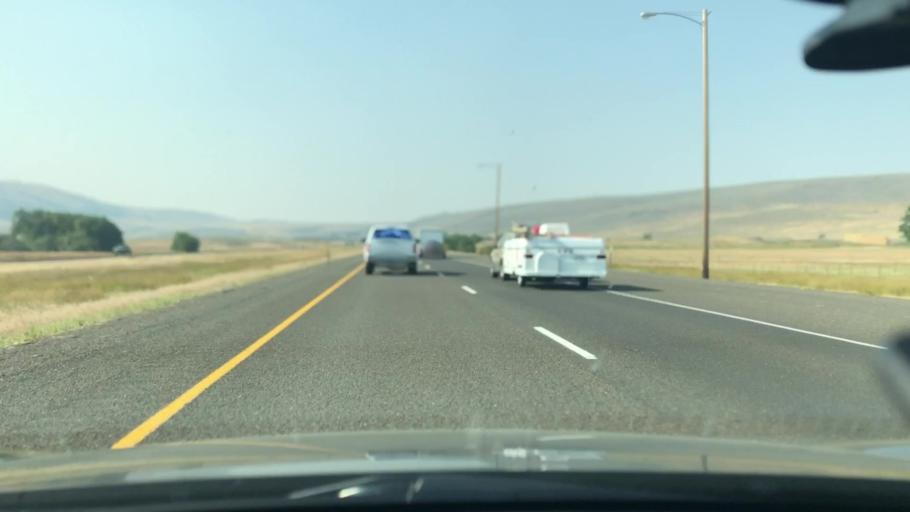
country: US
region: Oregon
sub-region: Union County
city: Union
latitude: 45.1163
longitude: -117.9598
